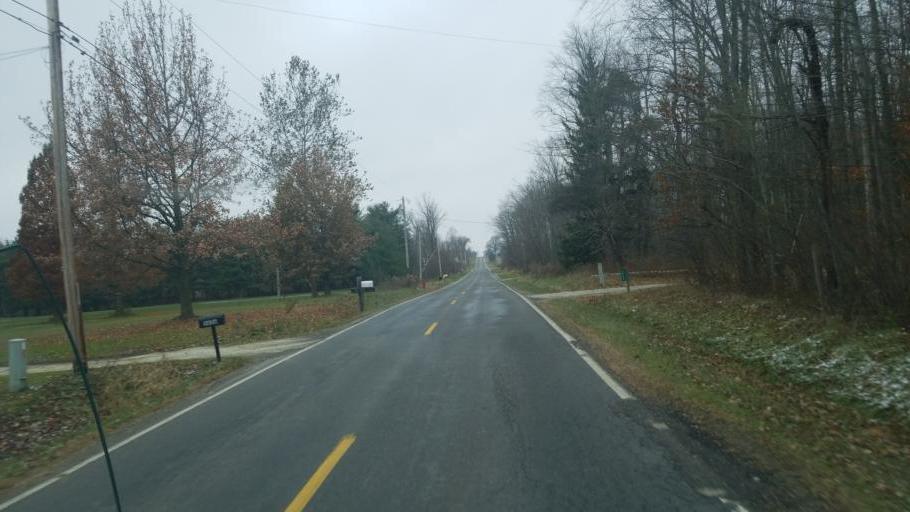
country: US
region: Ohio
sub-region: Medina County
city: Lodi
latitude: 41.1190
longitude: -82.0026
